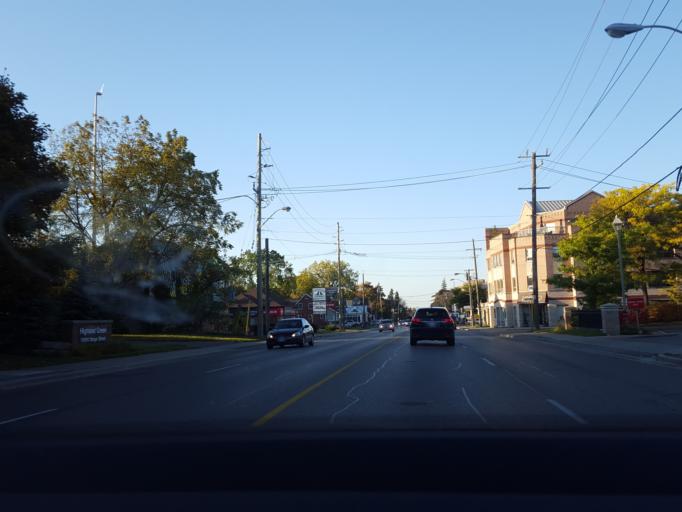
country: CA
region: Ontario
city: Newmarket
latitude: 43.9917
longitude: -79.4656
